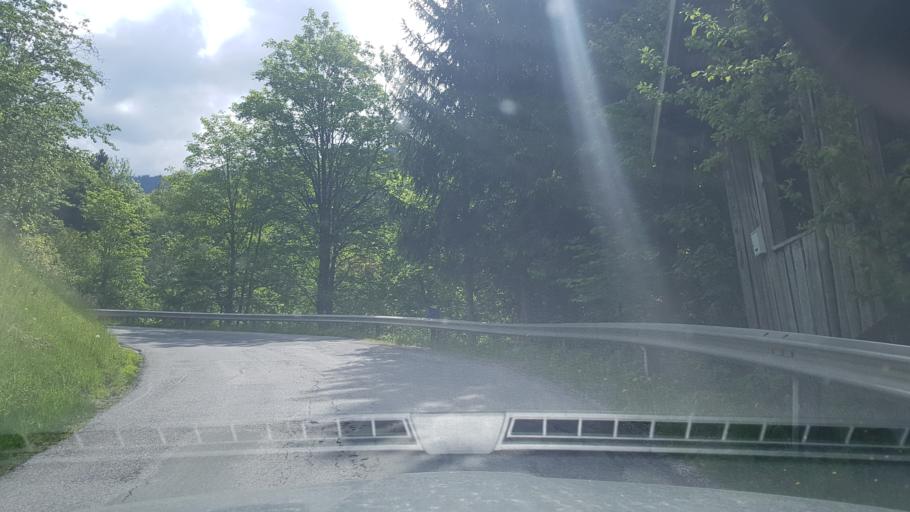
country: AT
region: Salzburg
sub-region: Politischer Bezirk Sankt Johann im Pongau
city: Dorfgastein
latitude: 47.2488
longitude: 13.1113
